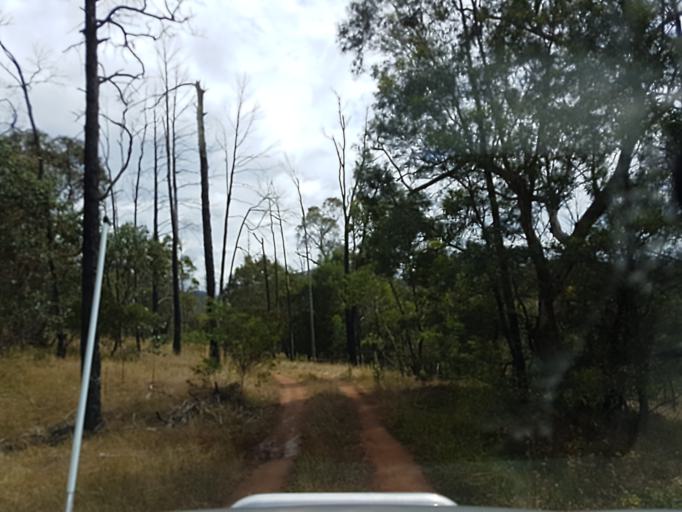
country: AU
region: New South Wales
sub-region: Snowy River
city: Jindabyne
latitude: -36.9324
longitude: 148.4001
